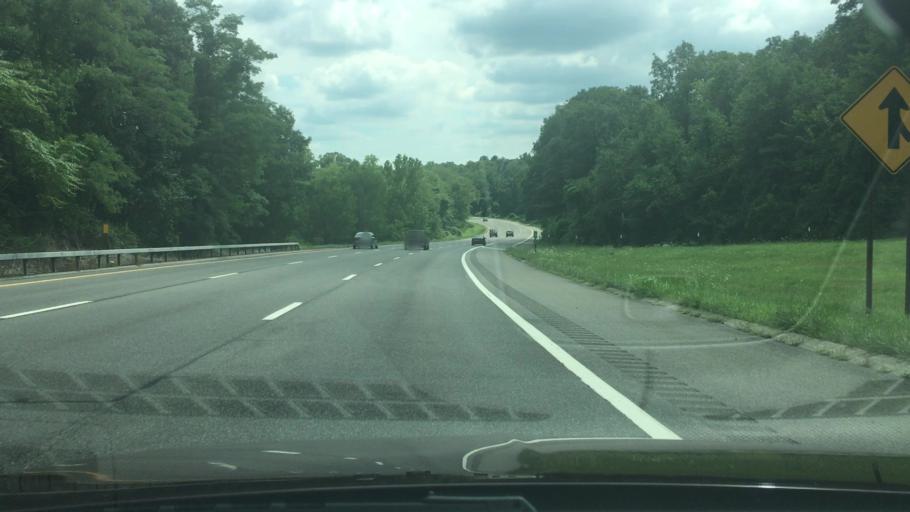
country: US
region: New York
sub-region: Westchester County
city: Yorktown Heights
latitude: 41.2127
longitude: -73.8104
